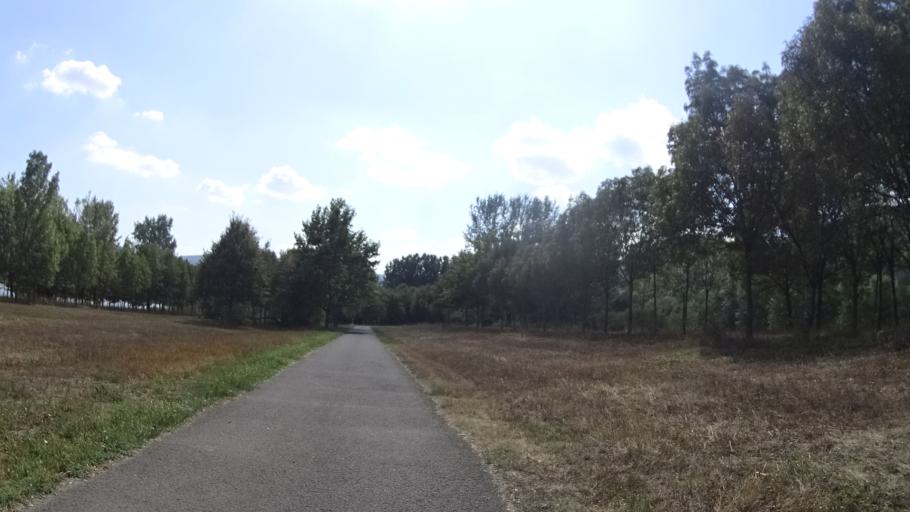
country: HU
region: Pest
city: Nagymaros
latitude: 47.7785
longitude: 18.9540
